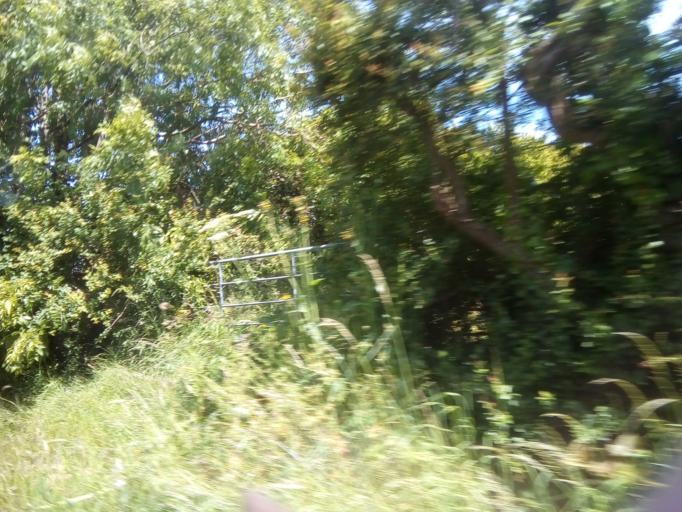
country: IE
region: Leinster
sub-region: Loch Garman
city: Loch Garman
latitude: 52.2354
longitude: -6.5962
